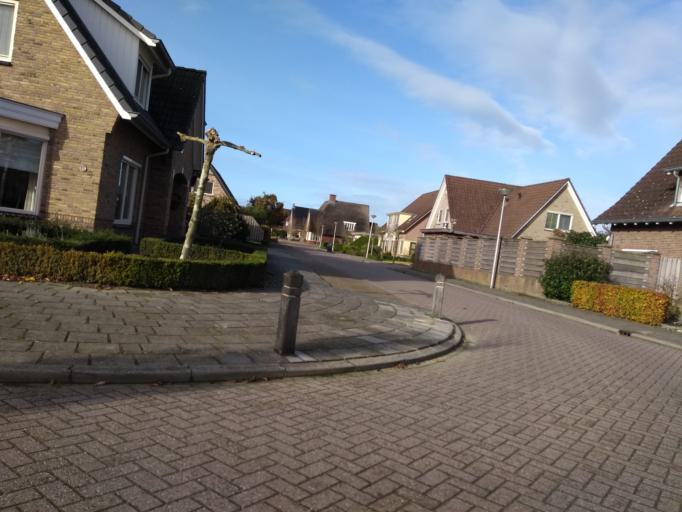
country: NL
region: Overijssel
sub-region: Gemeente Almelo
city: Almelo
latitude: 52.3842
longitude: 6.7142
